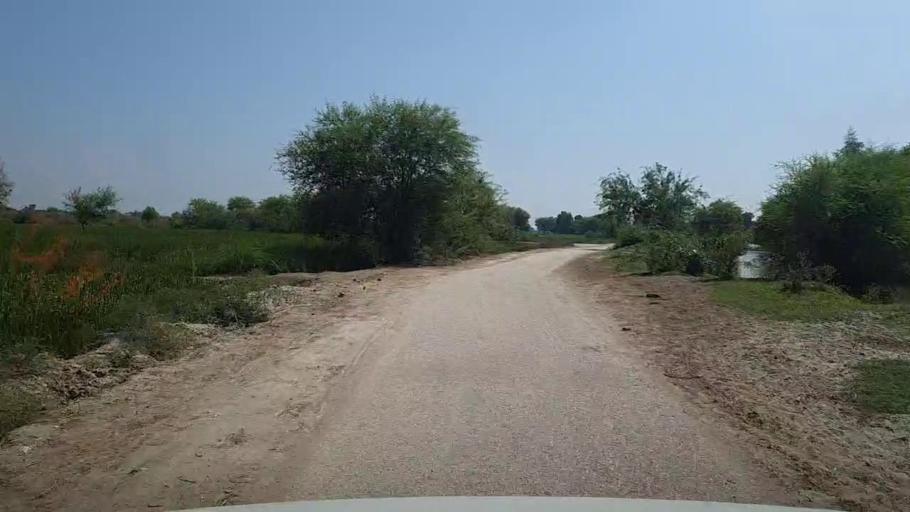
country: PK
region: Sindh
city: Kandhkot
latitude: 28.2841
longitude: 69.3543
